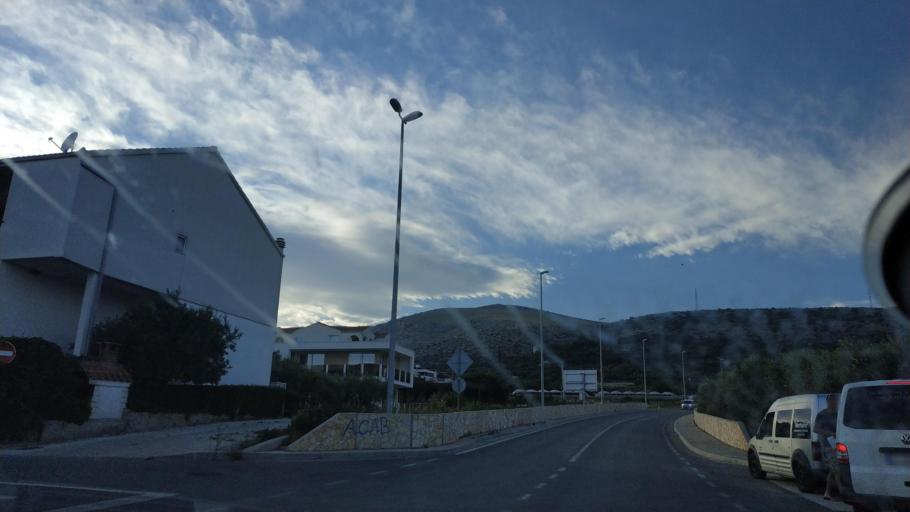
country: HR
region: Splitsko-Dalmatinska
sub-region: Grad Trogir
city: Trogir
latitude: 43.5243
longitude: 16.2636
